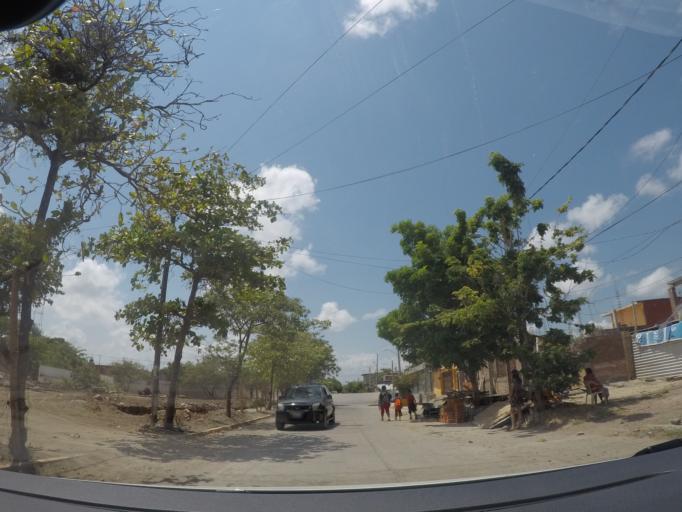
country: MX
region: Oaxaca
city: Juchitan de Zaragoza
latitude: 16.4397
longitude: -95.0180
